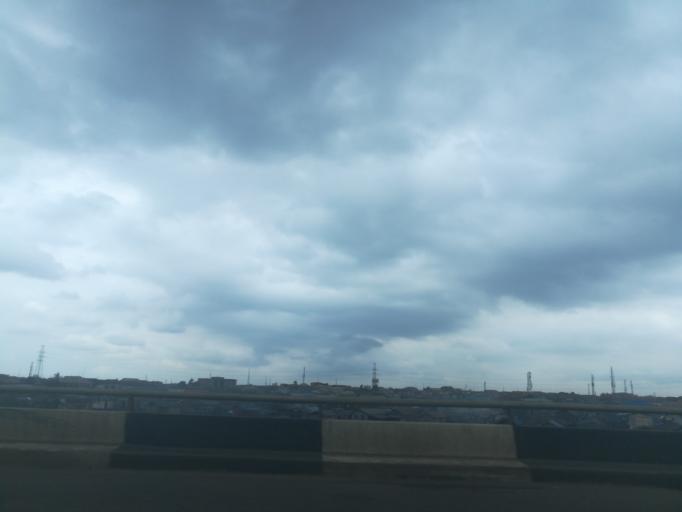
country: NG
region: Lagos
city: Somolu
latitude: 6.5329
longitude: 3.4014
